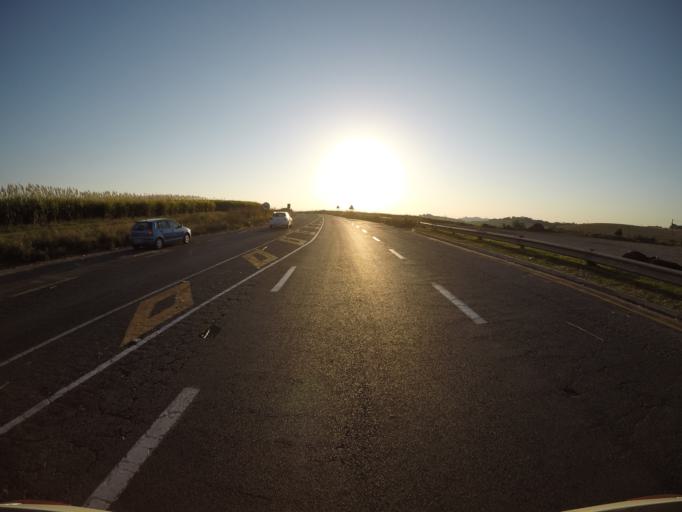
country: ZA
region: KwaZulu-Natal
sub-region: uThungulu District Municipality
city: eSikhawini
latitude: -28.9470
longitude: 31.7340
